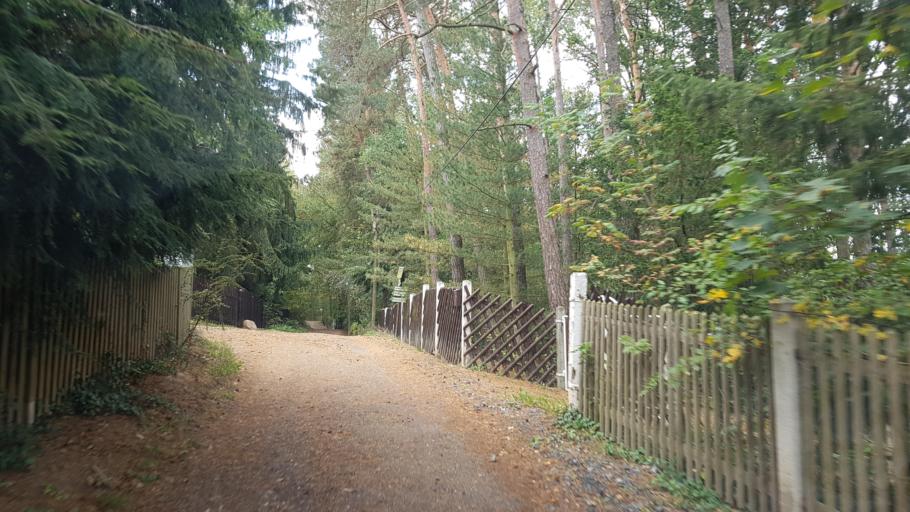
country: DE
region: Saxony
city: Dahlen
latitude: 51.3935
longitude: 12.9958
